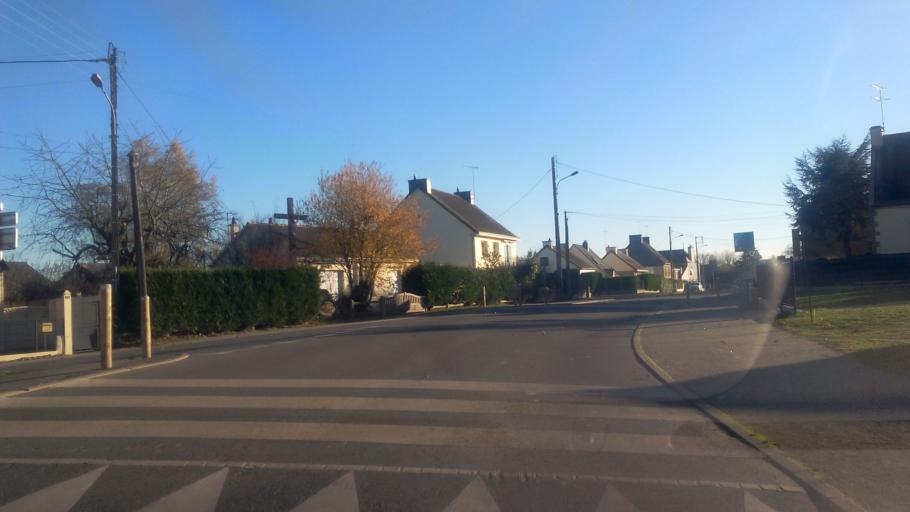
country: FR
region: Brittany
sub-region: Departement du Morbihan
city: Peillac
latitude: 47.7155
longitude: -2.2224
